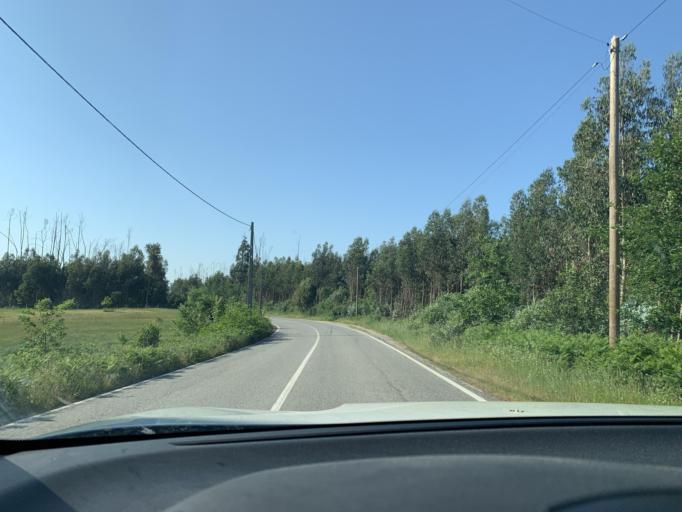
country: PT
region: Viseu
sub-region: Santa Comba Dao
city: Santa Comba Dao
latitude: 40.4517
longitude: -8.1031
